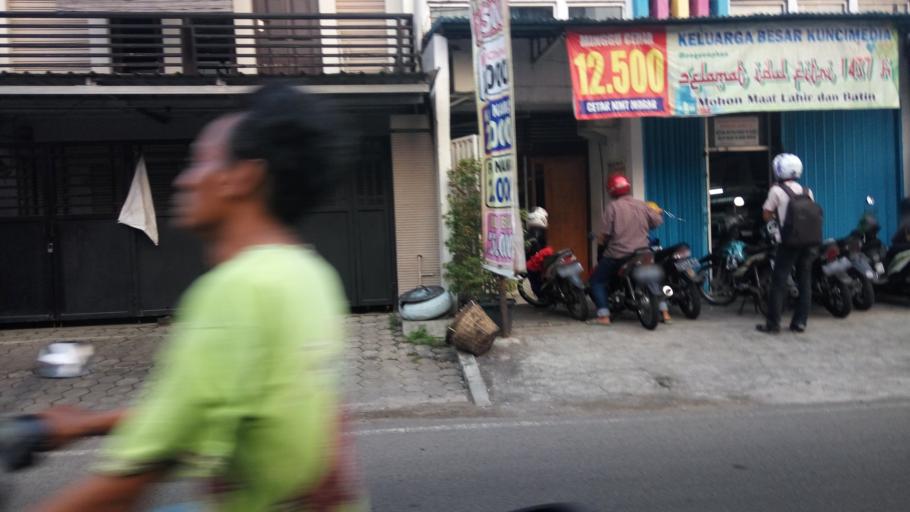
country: ID
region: Central Java
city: Semarang
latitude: -6.9885
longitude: 110.4044
